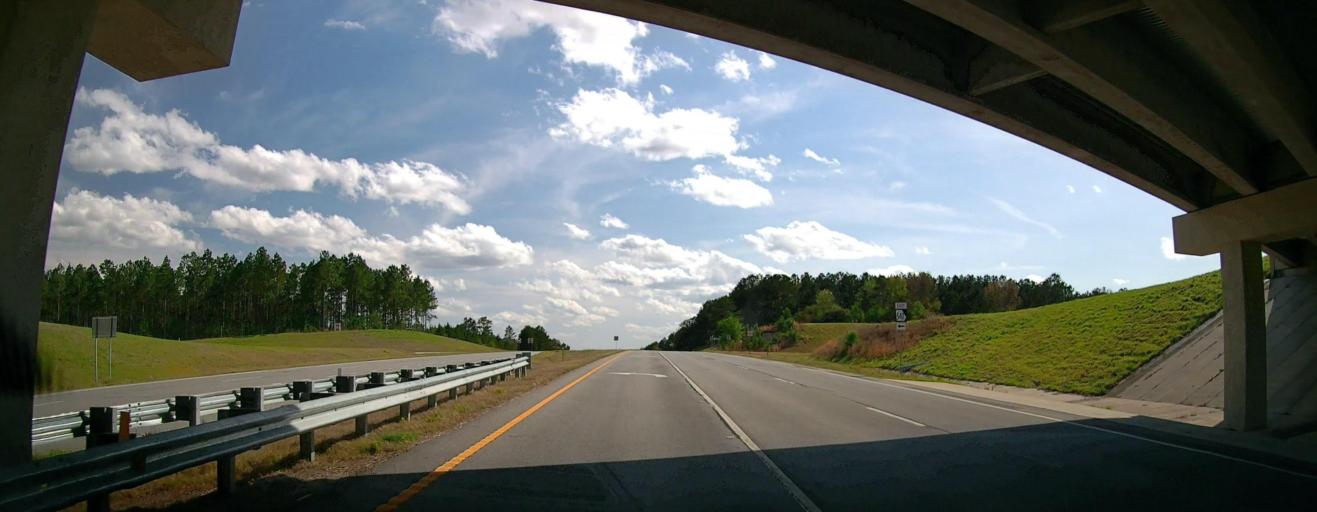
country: US
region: Georgia
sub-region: Baldwin County
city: Hardwick
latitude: 32.9792
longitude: -83.2141
